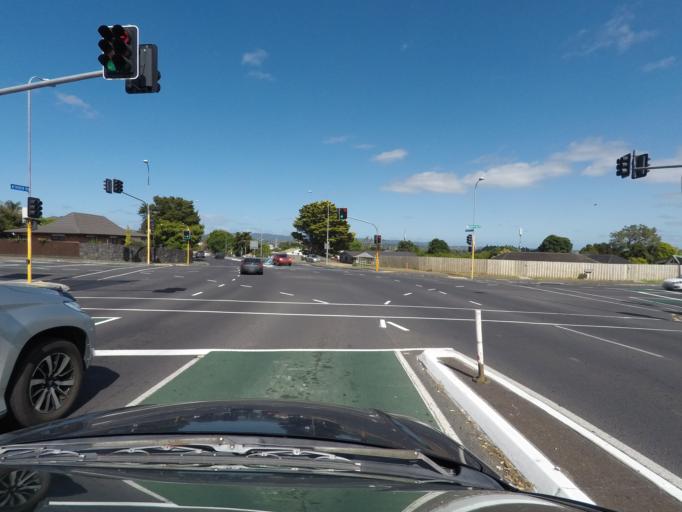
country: NZ
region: Auckland
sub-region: Auckland
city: Rosebank
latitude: -36.9060
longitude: 174.7019
